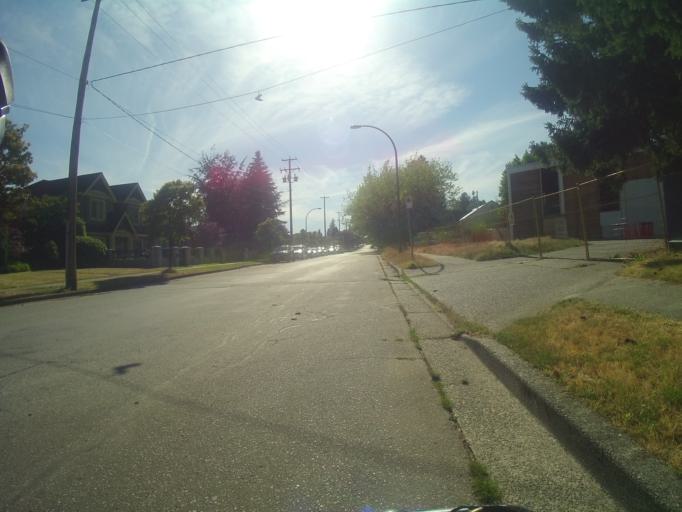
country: CA
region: British Columbia
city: Vancouver
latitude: 49.2170
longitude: -123.1180
